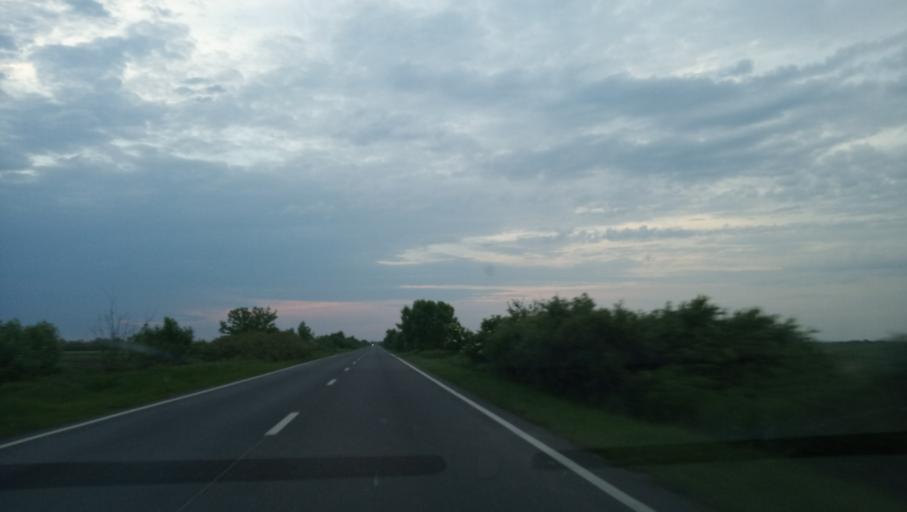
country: RO
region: Timis
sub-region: Comuna Jebel
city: Jebel
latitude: 45.5365
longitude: 21.2277
